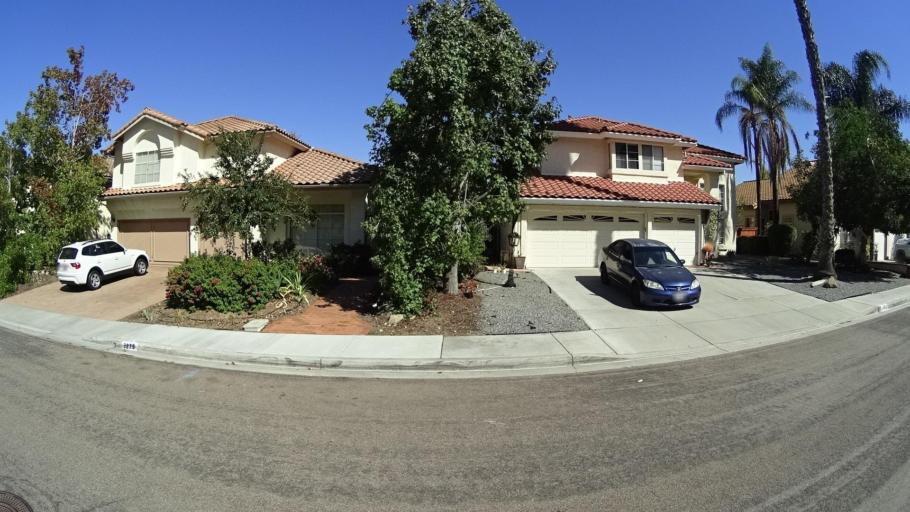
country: US
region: California
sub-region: San Diego County
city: Rancho San Diego
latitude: 32.7339
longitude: -116.9128
